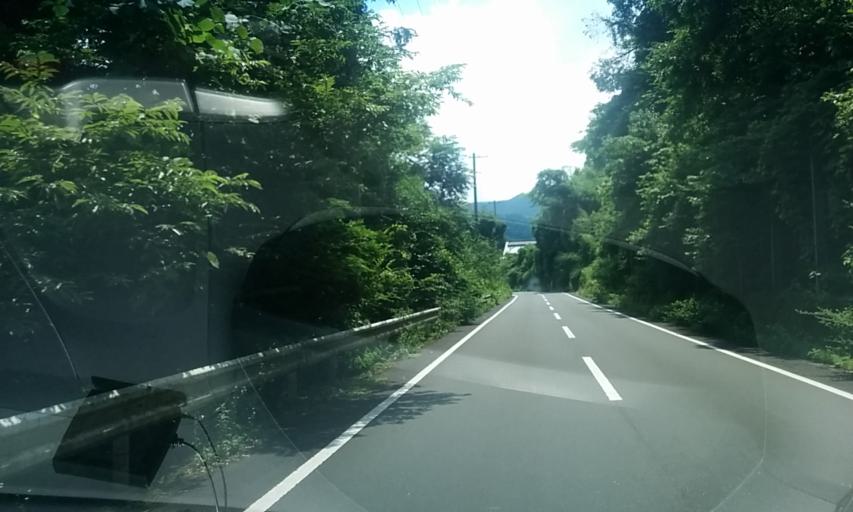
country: JP
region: Kyoto
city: Ayabe
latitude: 35.1842
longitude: 135.2766
